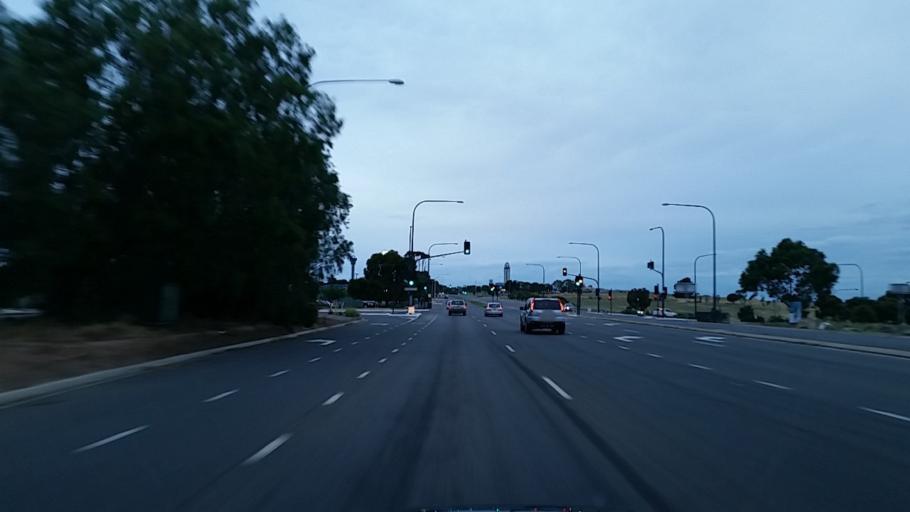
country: AU
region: South Australia
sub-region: Marion
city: Happy Valley
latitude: -35.0799
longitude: 138.5156
